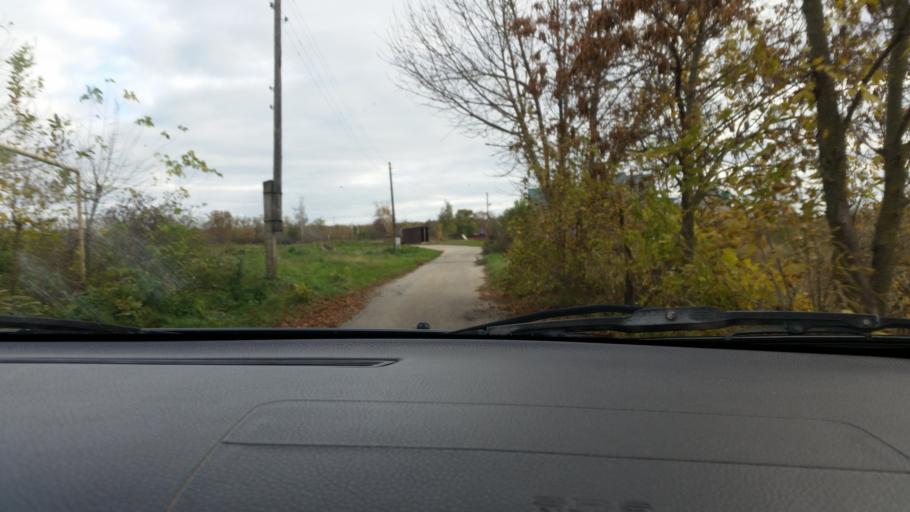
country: RU
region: Lipetsk
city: Gryazi
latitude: 52.4508
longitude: 39.9848
